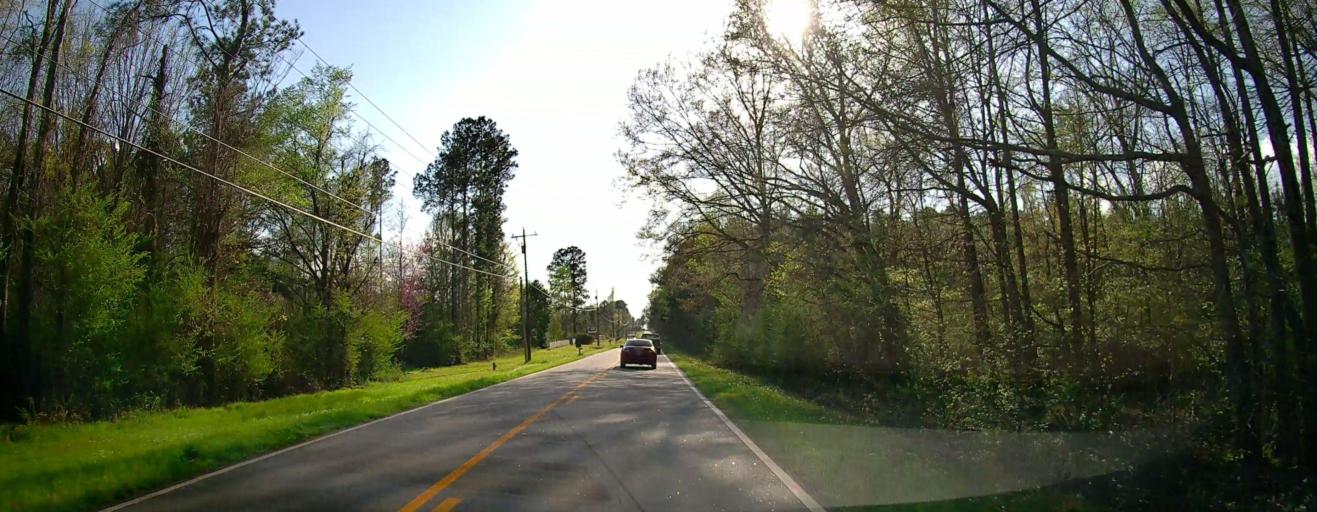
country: US
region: Georgia
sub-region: Putnam County
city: Eatonton
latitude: 33.1987
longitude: -83.3867
